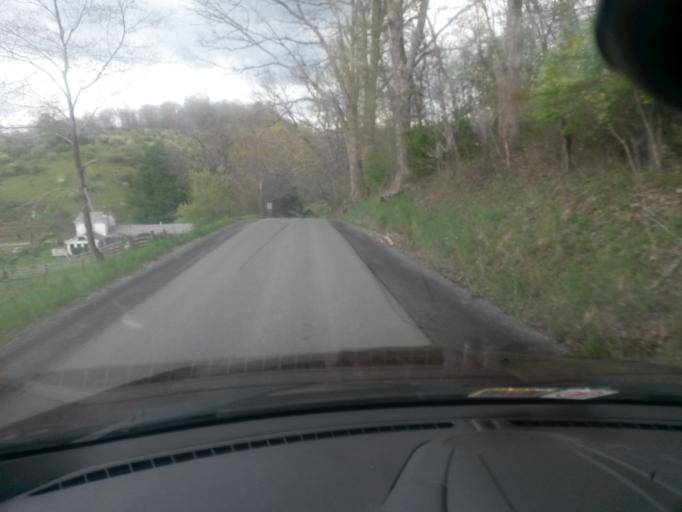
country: US
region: West Virginia
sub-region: Greenbrier County
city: Lewisburg
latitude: 37.9402
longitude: -80.4428
